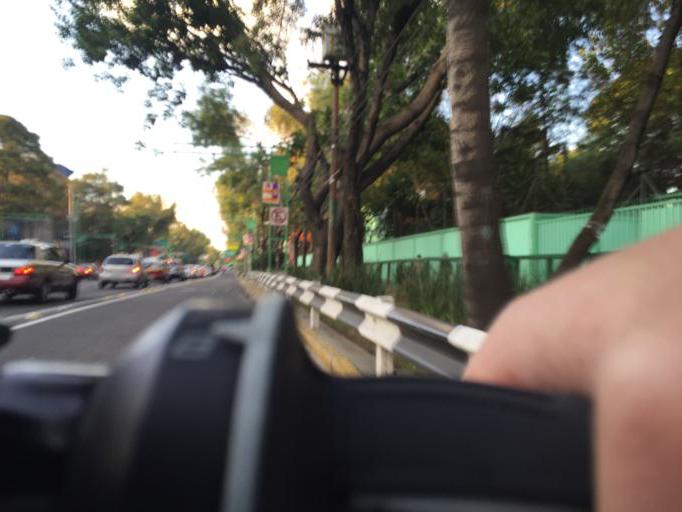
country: MX
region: Mexico City
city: Colonia Nativitas
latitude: 19.3760
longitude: -99.1488
